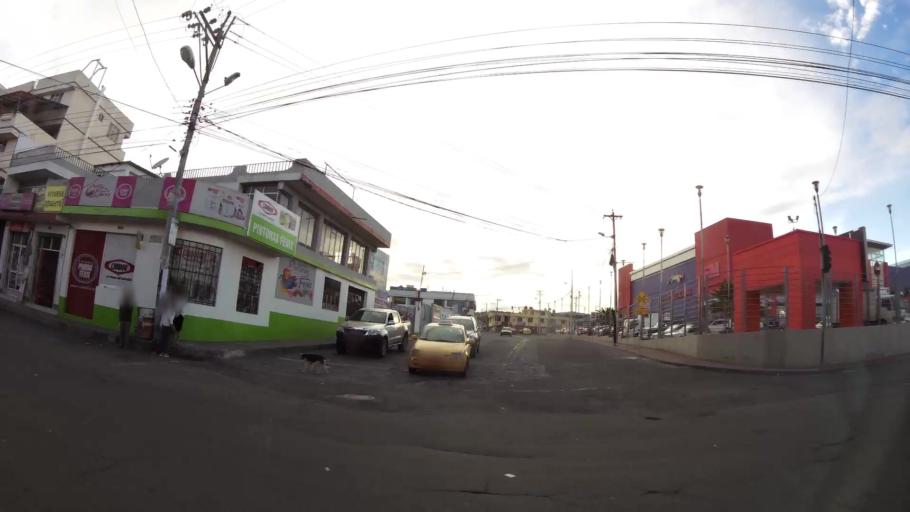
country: EC
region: Cotopaxi
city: Latacunga
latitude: -0.9270
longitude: -78.6248
